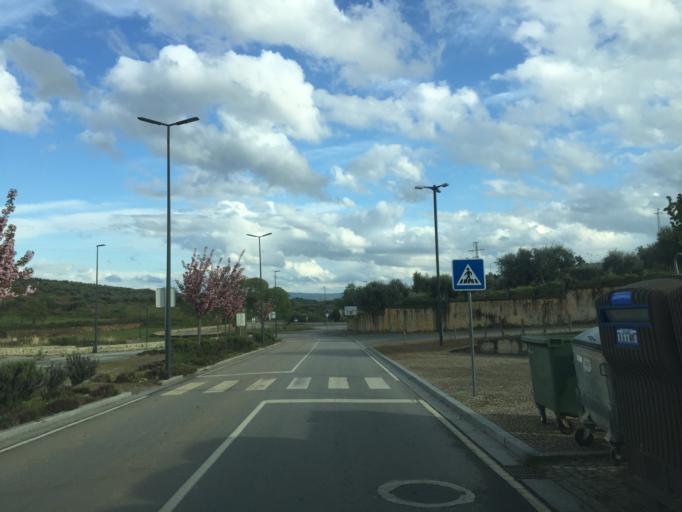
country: PT
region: Braganca
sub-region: Alfandega da Fe
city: Alfandega da Fe
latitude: 41.3409
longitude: -6.9609
